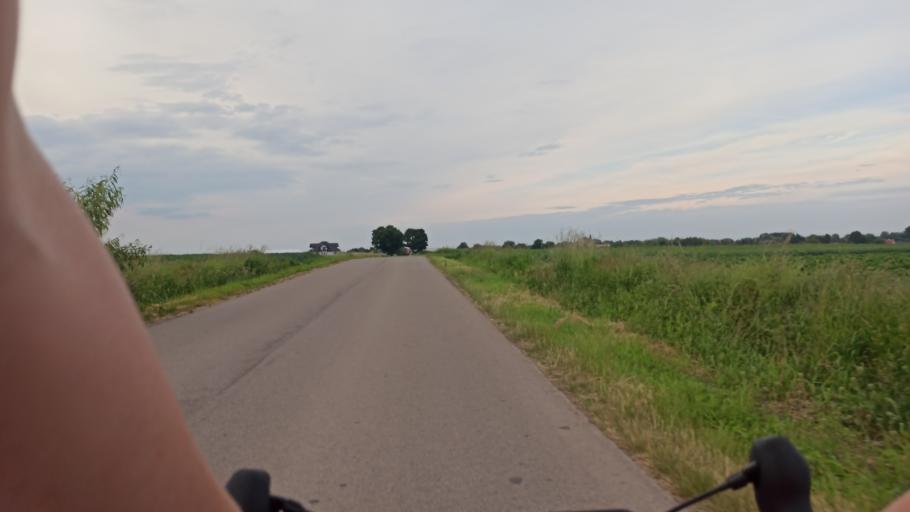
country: PL
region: Subcarpathian Voivodeship
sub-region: Powiat jaroslawski
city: Radymno
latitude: 49.9266
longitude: 22.8041
